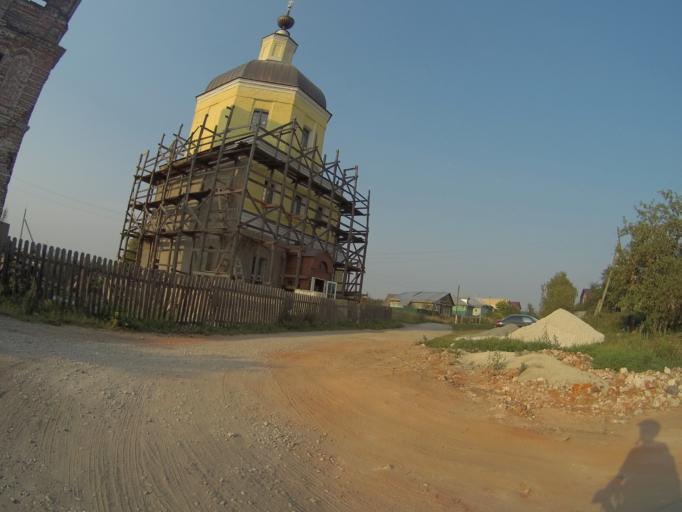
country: RU
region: Vladimir
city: Orgtrud
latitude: 56.2064
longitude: 40.5836
